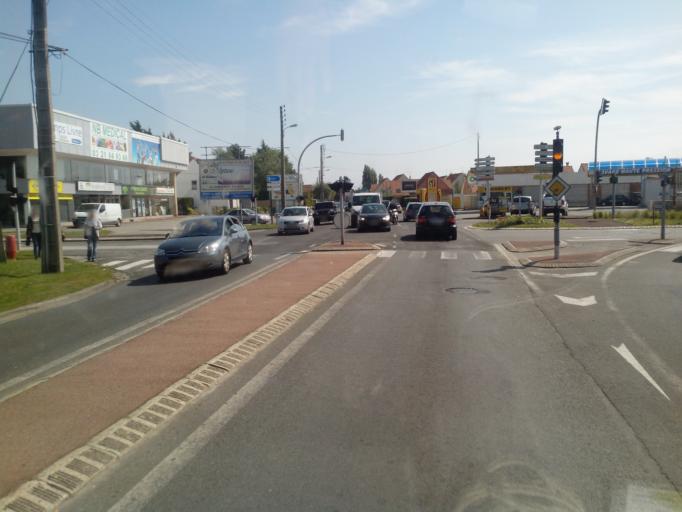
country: FR
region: Nord-Pas-de-Calais
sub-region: Departement du Pas-de-Calais
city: Berck
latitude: 50.4145
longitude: 1.5940
